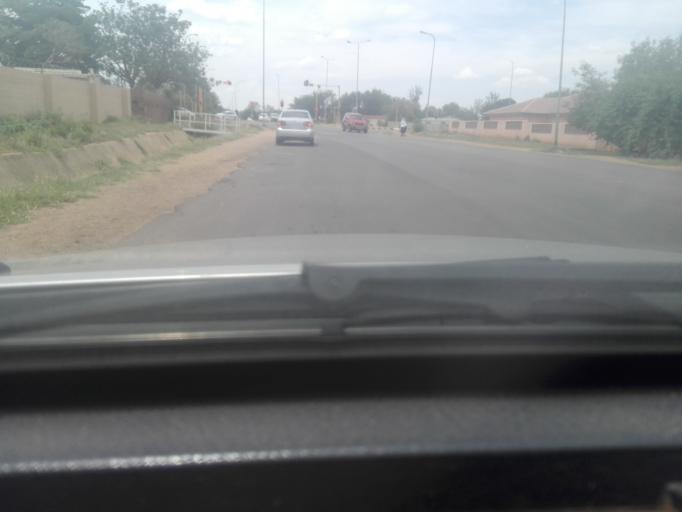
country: BW
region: South East
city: Gaborone
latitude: -24.6273
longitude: 25.9436
